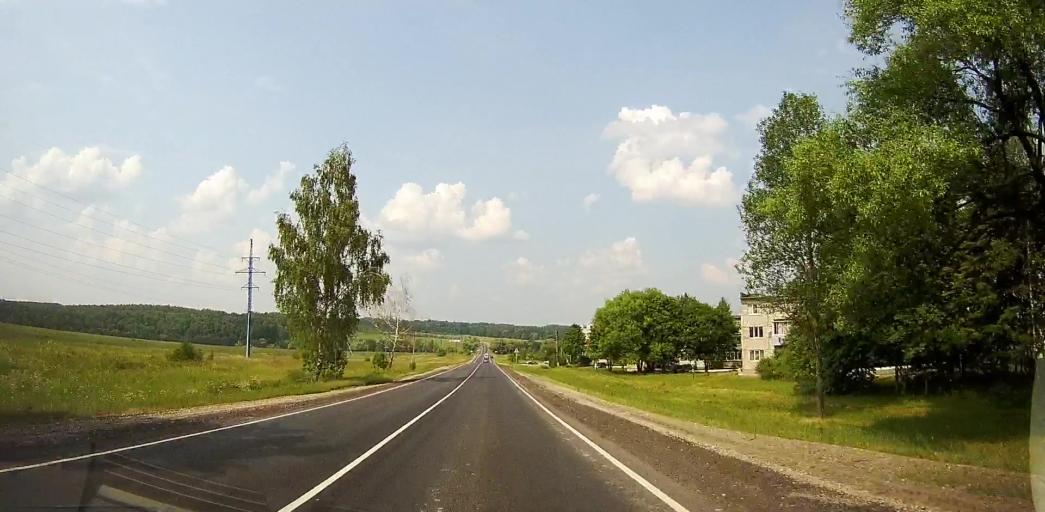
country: RU
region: Moskovskaya
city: Stupino
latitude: 54.9392
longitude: 38.1340
